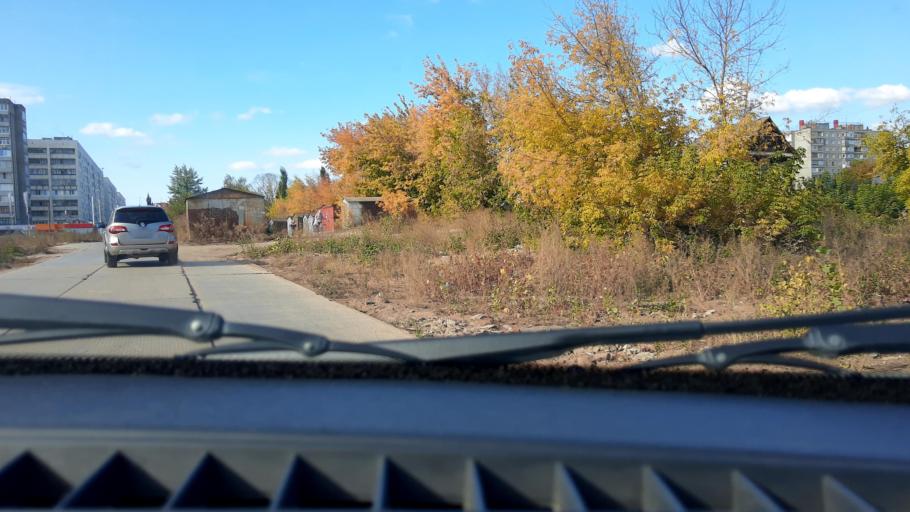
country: RU
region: Bashkortostan
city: Ufa
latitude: 54.7794
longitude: 56.1342
